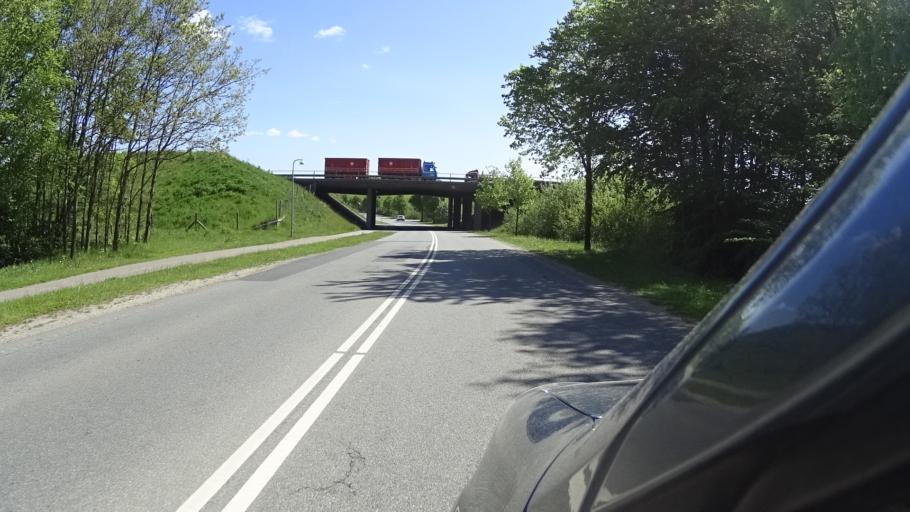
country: DK
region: South Denmark
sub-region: Vejle Kommune
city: Vejle
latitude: 55.6720
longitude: 9.5519
